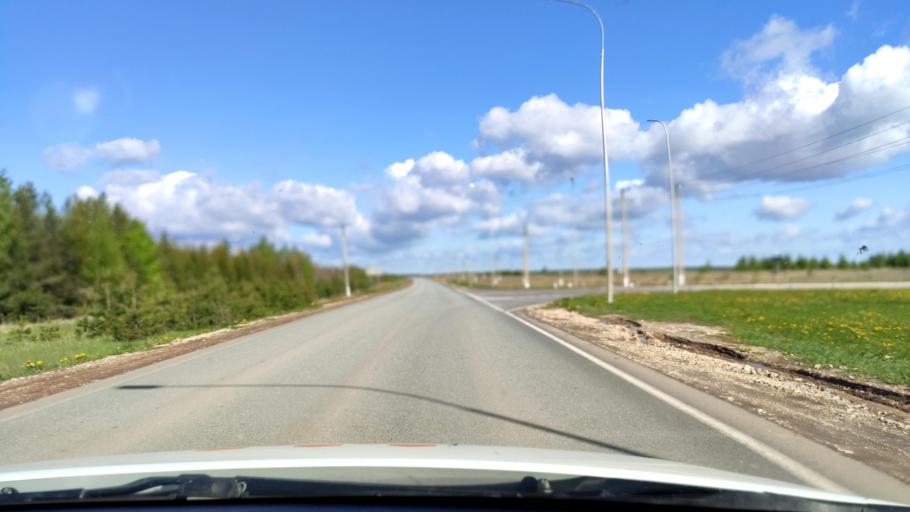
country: RU
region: Tatarstan
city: Sviyazhsk
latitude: 55.7372
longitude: 48.7369
